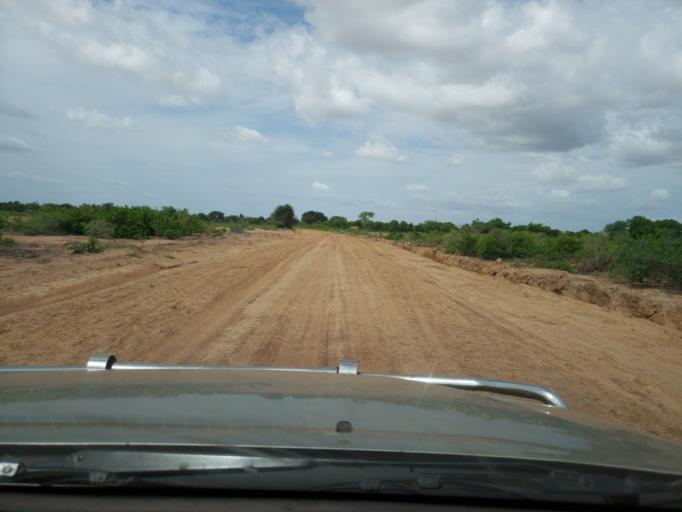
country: ML
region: Segou
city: Bla
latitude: 12.7104
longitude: -5.6906
